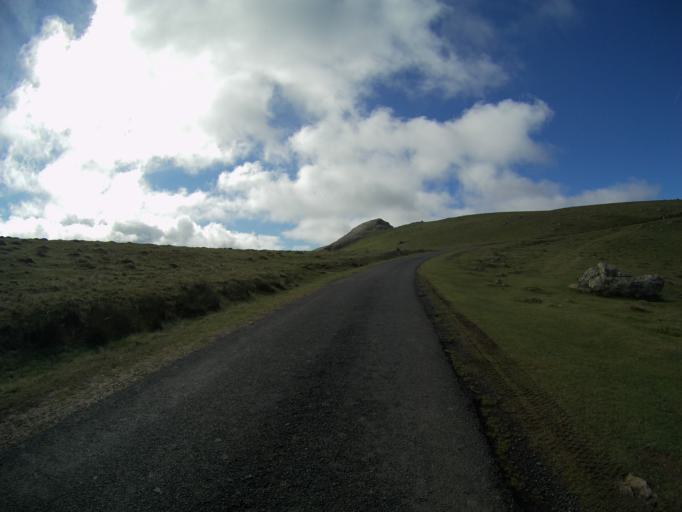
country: FR
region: Aquitaine
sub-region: Departement des Pyrenees-Atlantiques
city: Saint-Jean-Pied-de-Port
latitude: 43.0718
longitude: -1.2665
